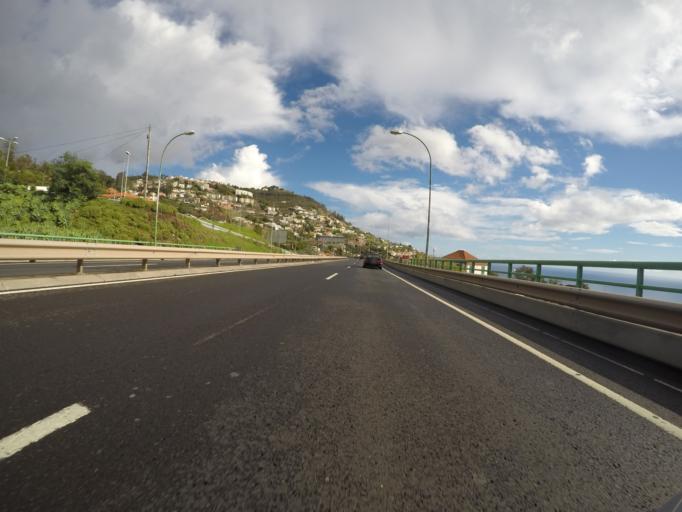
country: PT
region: Madeira
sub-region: Funchal
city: Nossa Senhora do Monte
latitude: 32.6561
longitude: -16.8842
